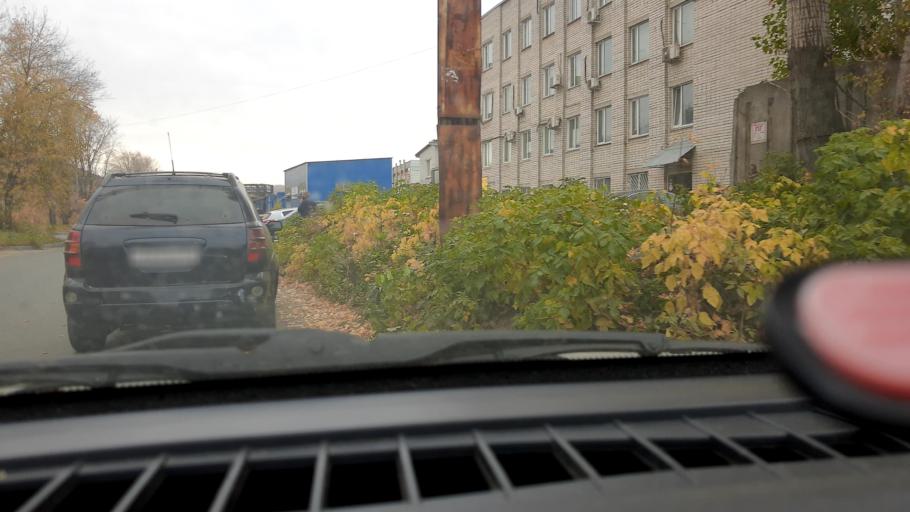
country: RU
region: Nizjnij Novgorod
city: Nizhniy Novgorod
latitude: 56.2548
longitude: 43.9197
